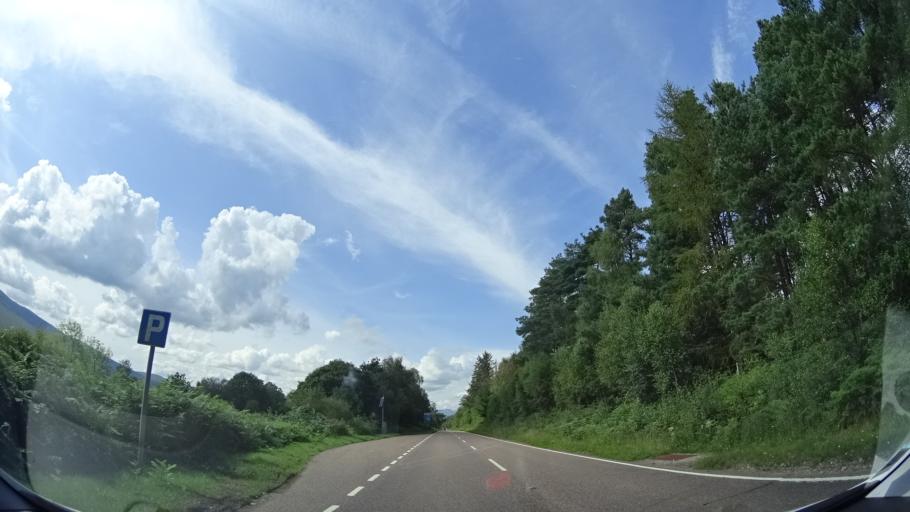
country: GB
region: Scotland
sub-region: Highland
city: Fort William
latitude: 56.8557
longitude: -5.2049
